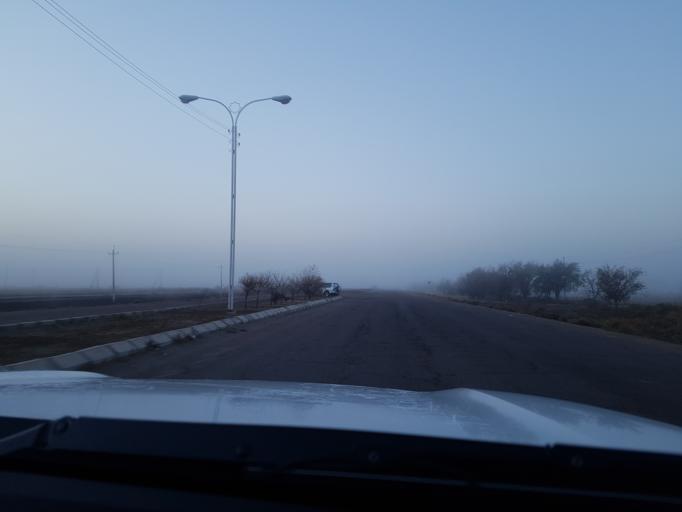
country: TM
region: Dasoguz
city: Koeneuergench
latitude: 41.7351
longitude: 58.6860
